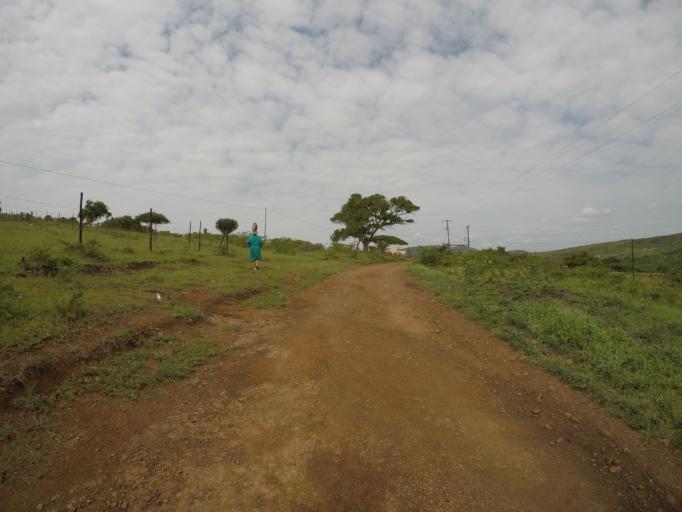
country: ZA
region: KwaZulu-Natal
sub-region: uThungulu District Municipality
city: Empangeni
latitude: -28.6230
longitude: 31.9017
